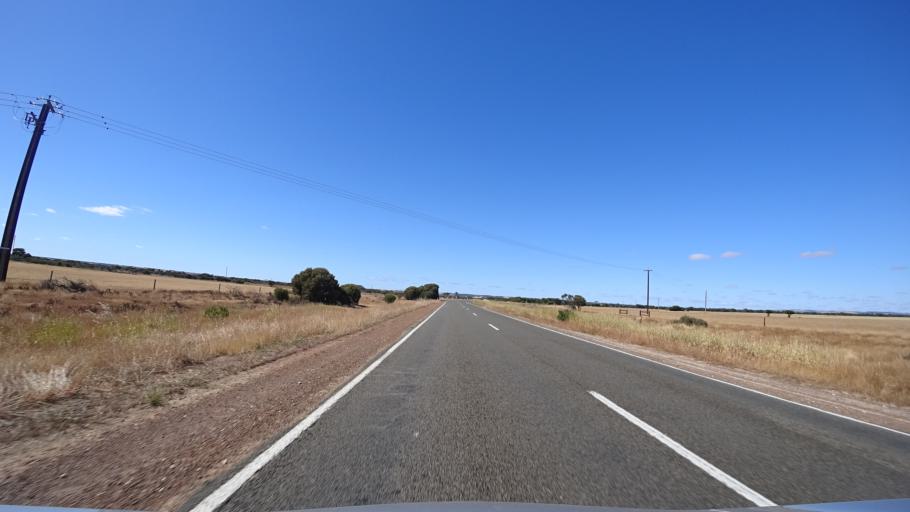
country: AU
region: South Australia
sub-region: Kangaroo Island
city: Kingscote
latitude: -35.6979
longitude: 137.5707
